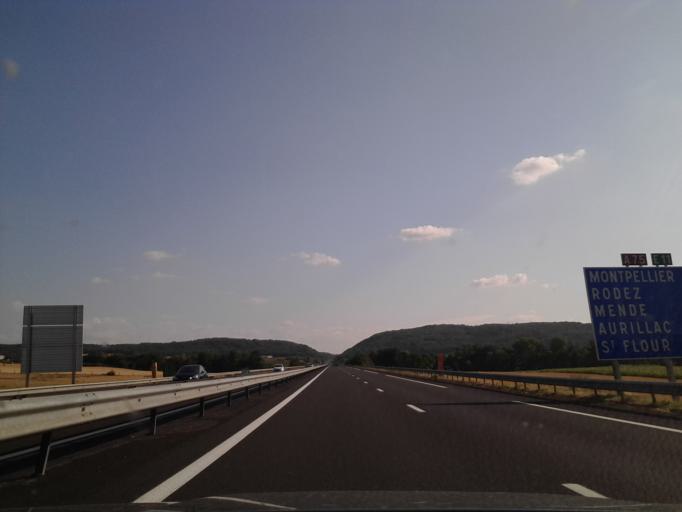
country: FR
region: Auvergne
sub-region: Departement de la Haute-Loire
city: Bournoncle-Saint-Pierre
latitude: 45.3266
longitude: 3.2656
